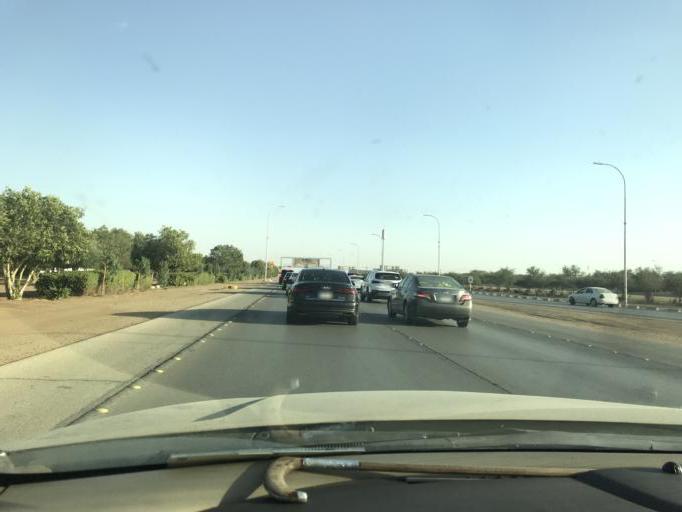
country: SA
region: Ar Riyad
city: Riyadh
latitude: 24.9408
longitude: 46.7091
